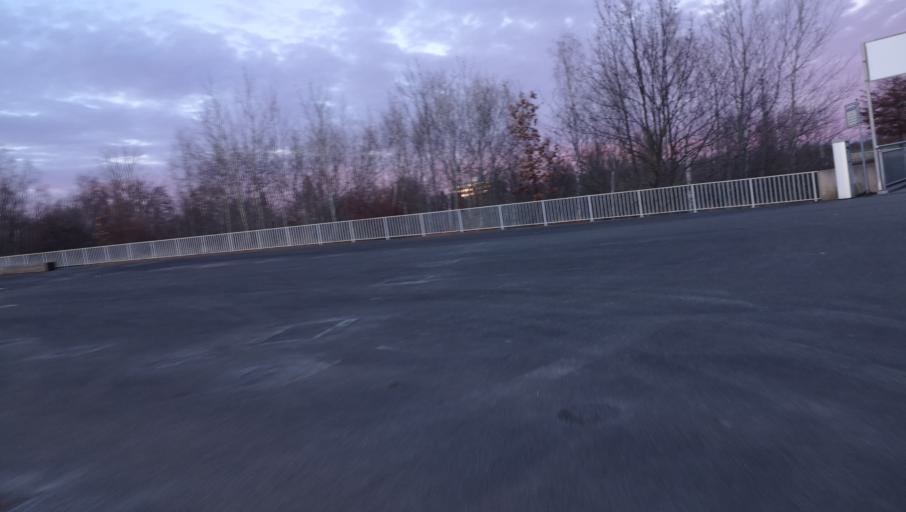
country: DE
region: Thuringia
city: Ronneburg
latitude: 50.8605
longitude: 12.1689
